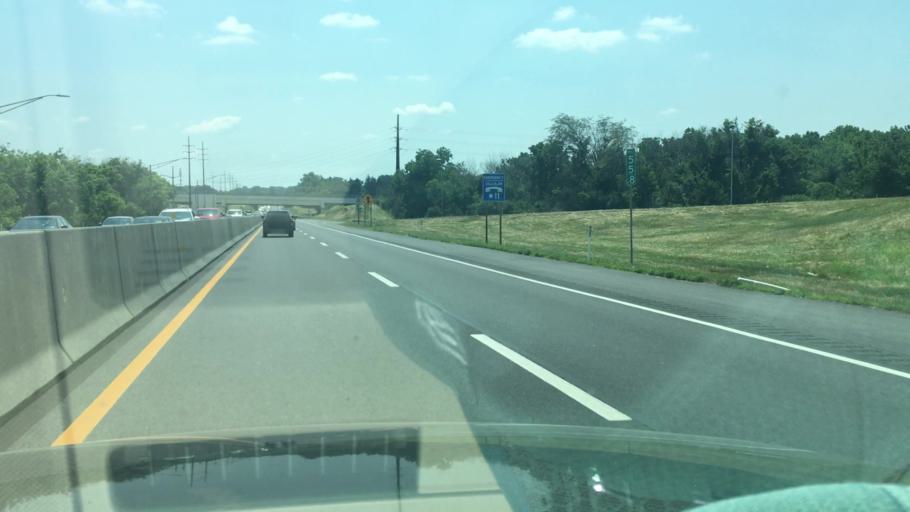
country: US
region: Pennsylvania
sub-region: Lehigh County
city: Wescosville
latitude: 40.5737
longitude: -75.5554
